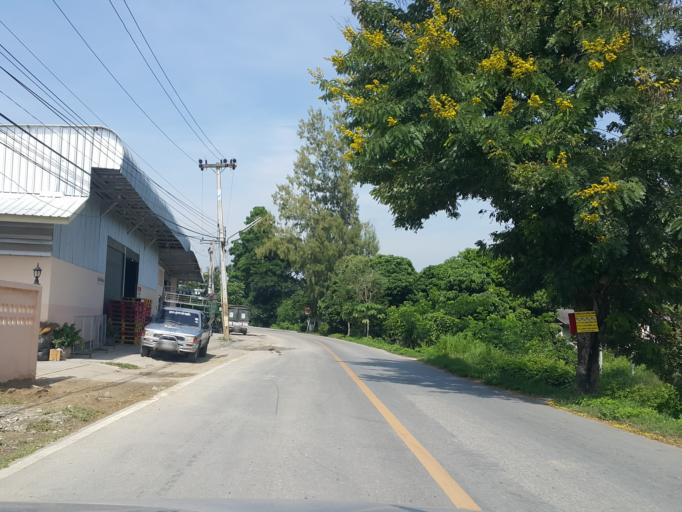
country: TH
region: Chiang Mai
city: Saraphi
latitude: 18.6835
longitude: 99.0634
